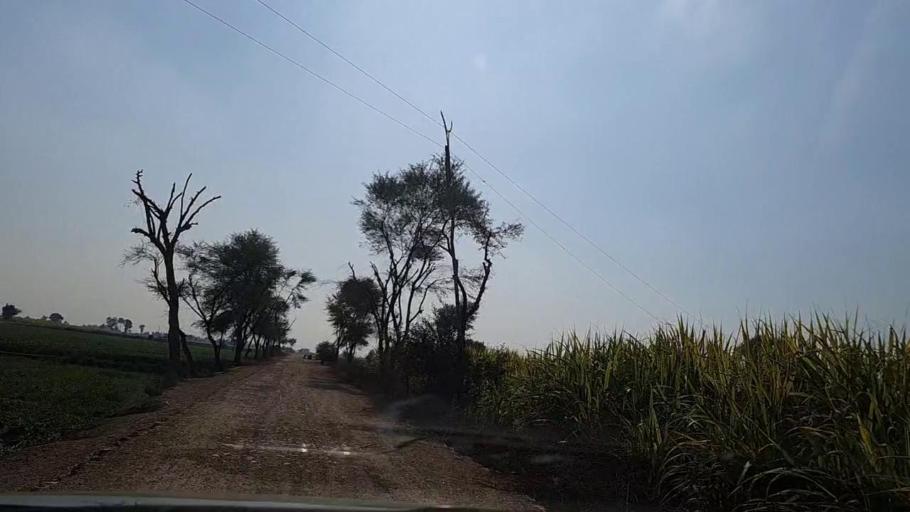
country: PK
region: Sindh
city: Daulatpur
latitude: 26.2872
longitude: 68.0537
